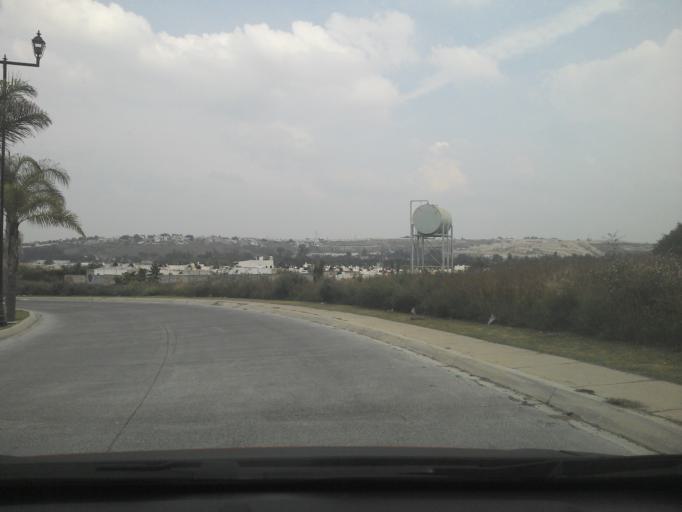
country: MX
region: Jalisco
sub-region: Tlajomulco de Zuniga
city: Lomas de San Agustin
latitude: 20.5297
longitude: -103.4740
